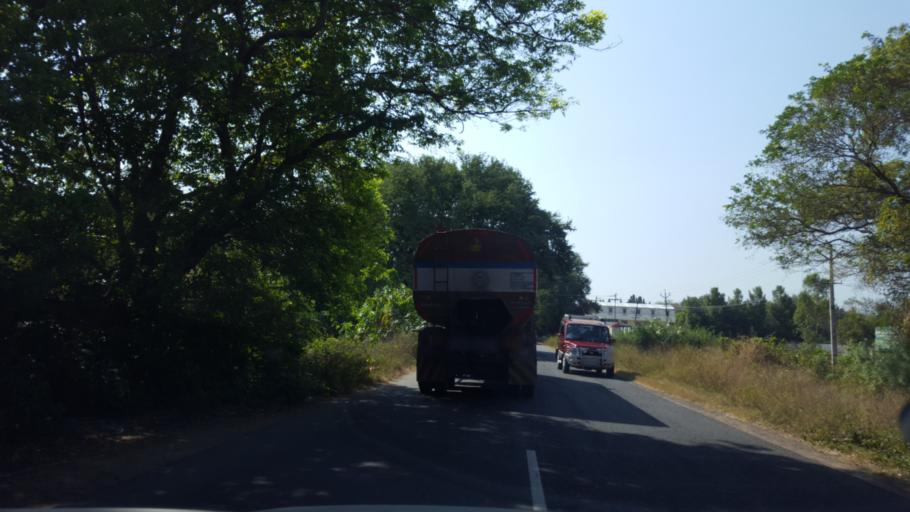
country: IN
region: Tamil Nadu
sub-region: Kancheepuram
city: Kanchipuram
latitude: 12.8624
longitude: 79.6690
